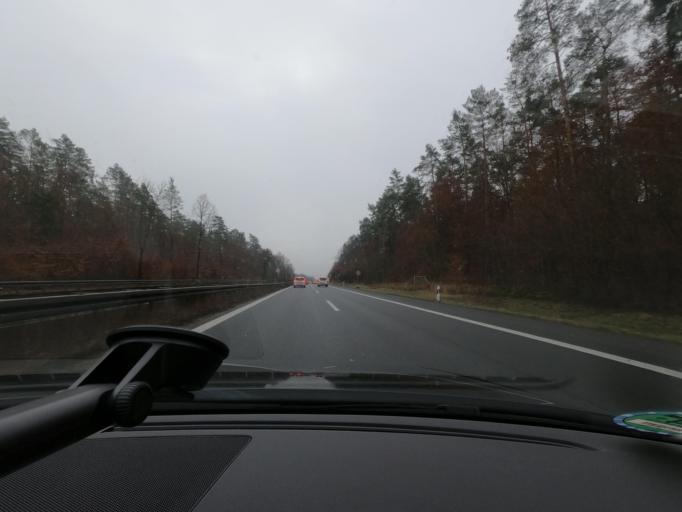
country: DE
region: Bavaria
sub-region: Upper Franconia
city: Memmelsdorf
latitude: 49.8930
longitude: 10.9491
